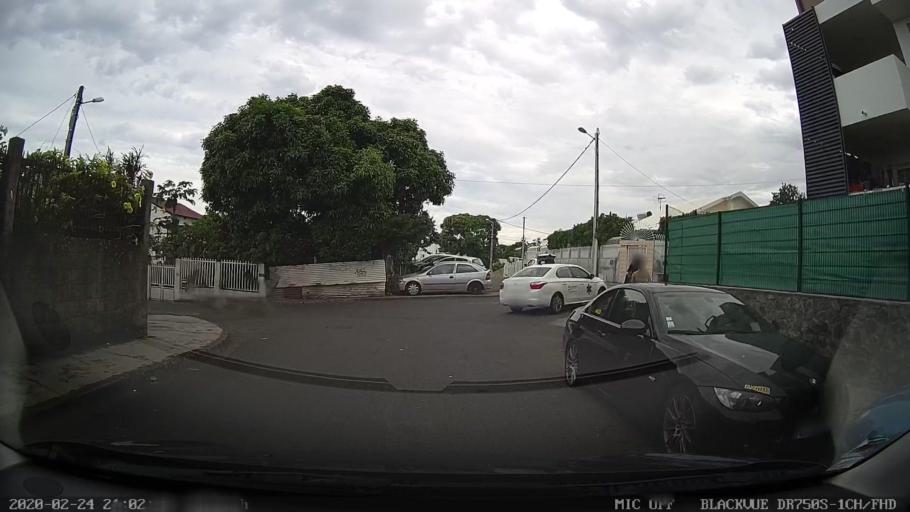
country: RE
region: Reunion
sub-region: Reunion
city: Saint-Denis
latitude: -20.8952
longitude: 55.4837
